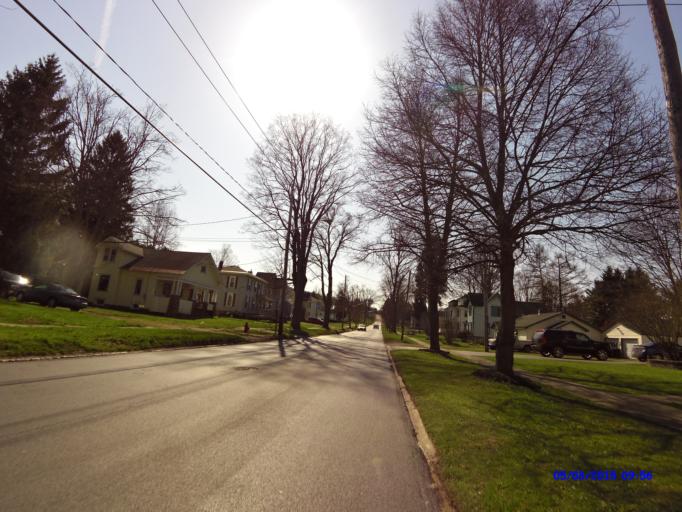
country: US
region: New York
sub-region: Cattaraugus County
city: Franklinville
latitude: 42.3351
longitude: -78.4491
